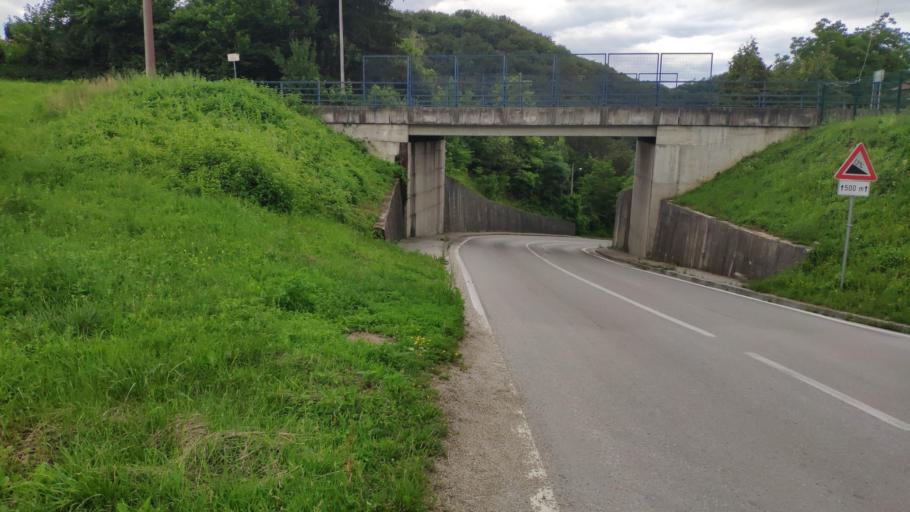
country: HR
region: Zagrebacka
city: Bregana
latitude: 45.8087
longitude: 15.6787
